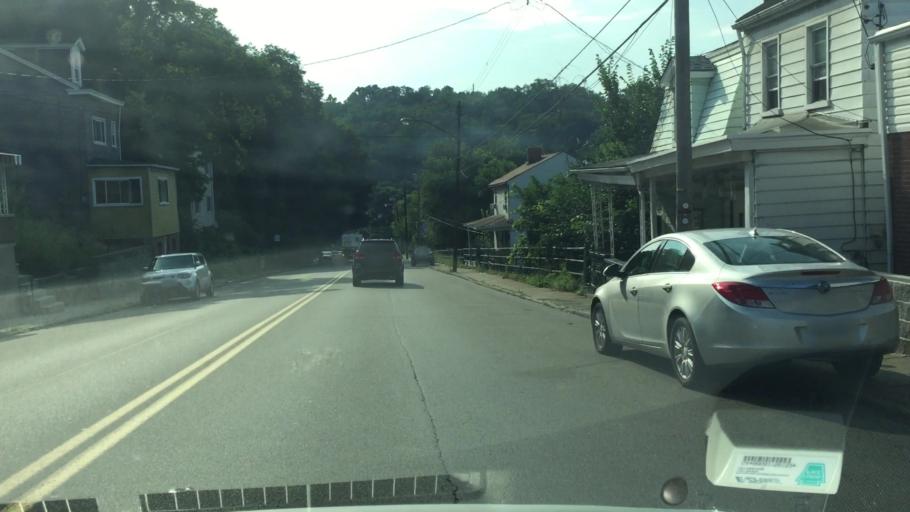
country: US
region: Pennsylvania
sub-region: Allegheny County
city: Mount Oliver
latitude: 40.4218
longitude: -79.9834
